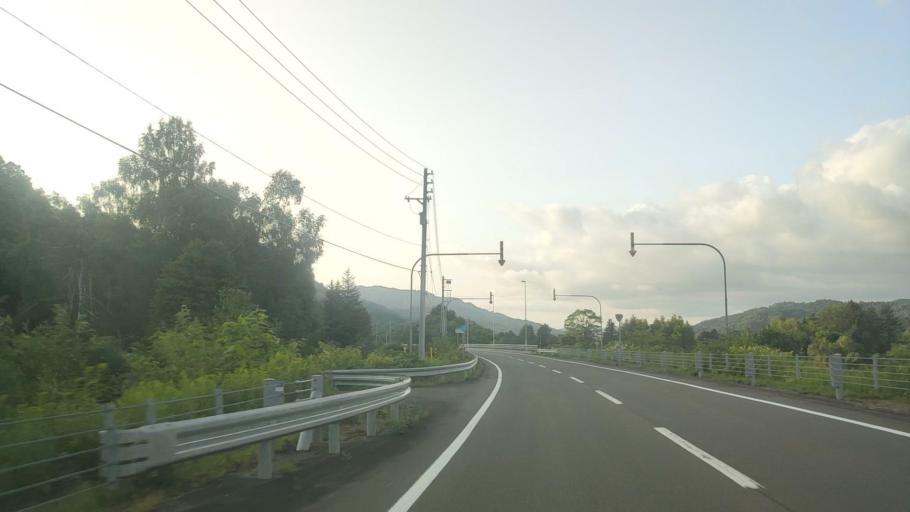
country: JP
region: Hokkaido
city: Bibai
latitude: 43.0776
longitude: 142.1018
